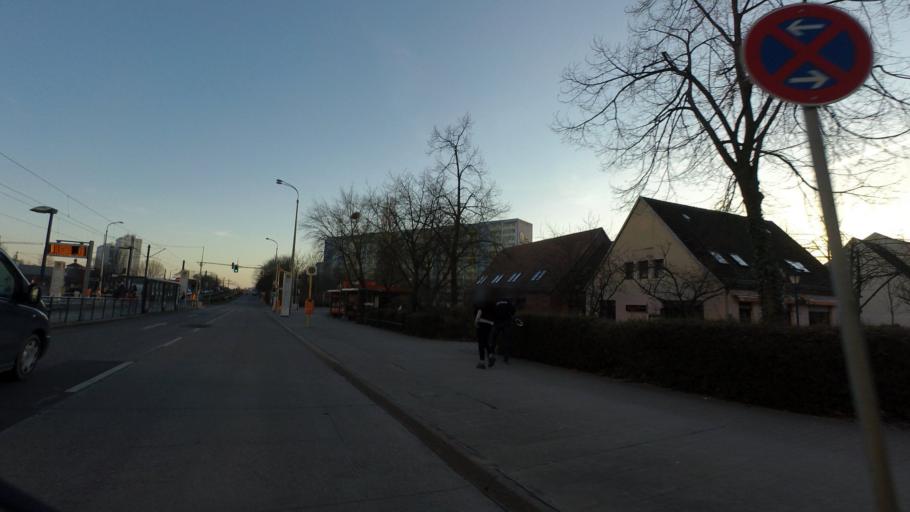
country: DE
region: Berlin
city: Marzahn
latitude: 52.5422
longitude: 13.5637
